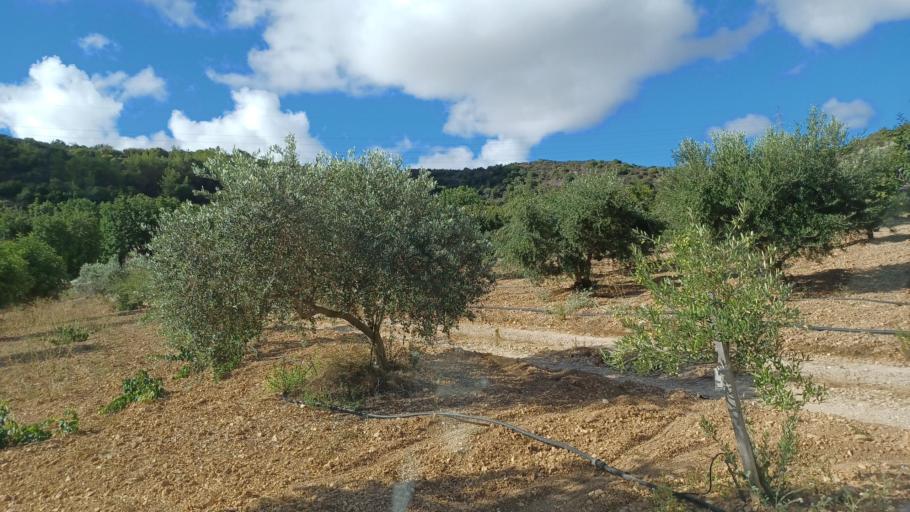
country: CY
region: Pafos
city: Tala
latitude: 34.8725
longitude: 32.4447
